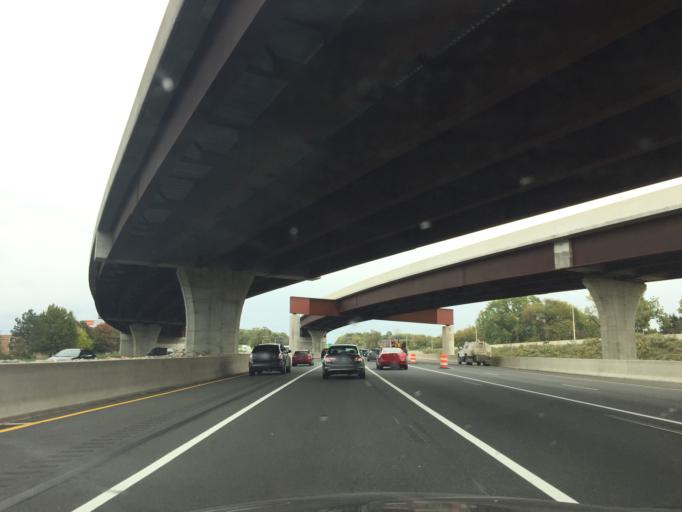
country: US
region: Delaware
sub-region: New Castle County
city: Newport
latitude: 39.6845
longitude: -75.6542
